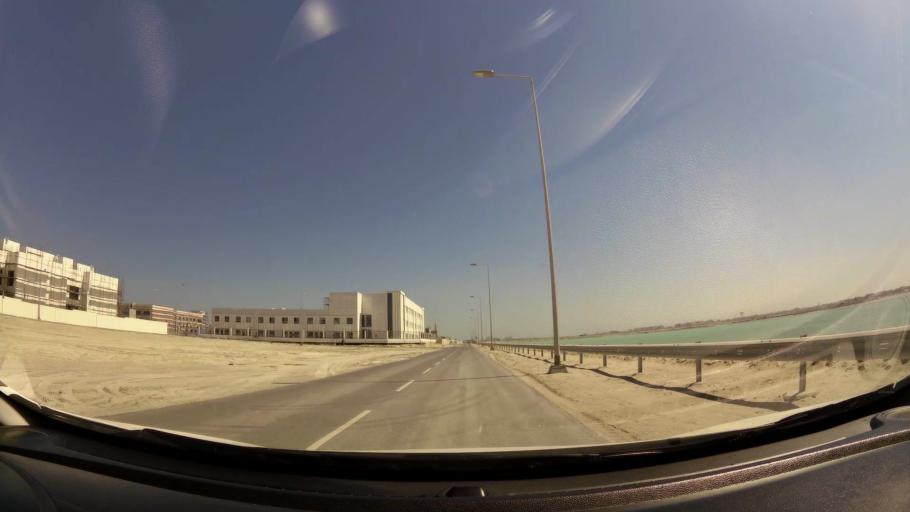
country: BH
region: Muharraq
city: Al Muharraq
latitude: 26.2992
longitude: 50.6344
